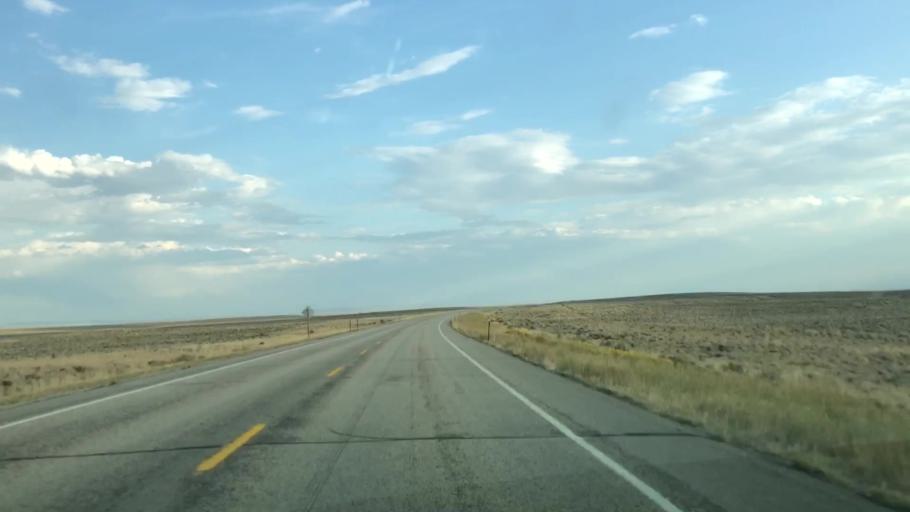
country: US
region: Wyoming
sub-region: Sweetwater County
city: North Rock Springs
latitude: 42.2561
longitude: -109.4690
